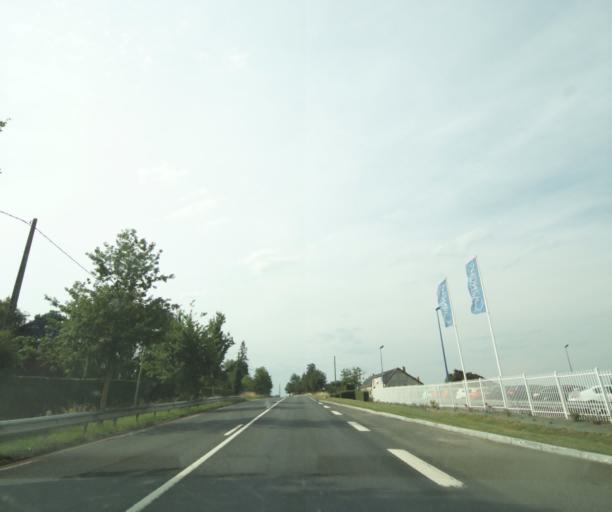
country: FR
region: Pays de la Loire
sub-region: Departement de la Sarthe
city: Ecommoy
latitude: 47.8411
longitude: 0.2620
